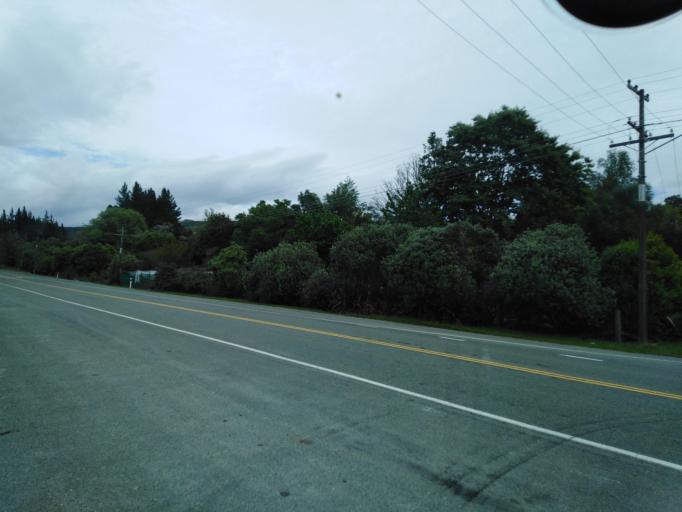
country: NZ
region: Tasman
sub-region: Tasman District
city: Wakefield
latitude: -41.4496
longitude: 172.9595
